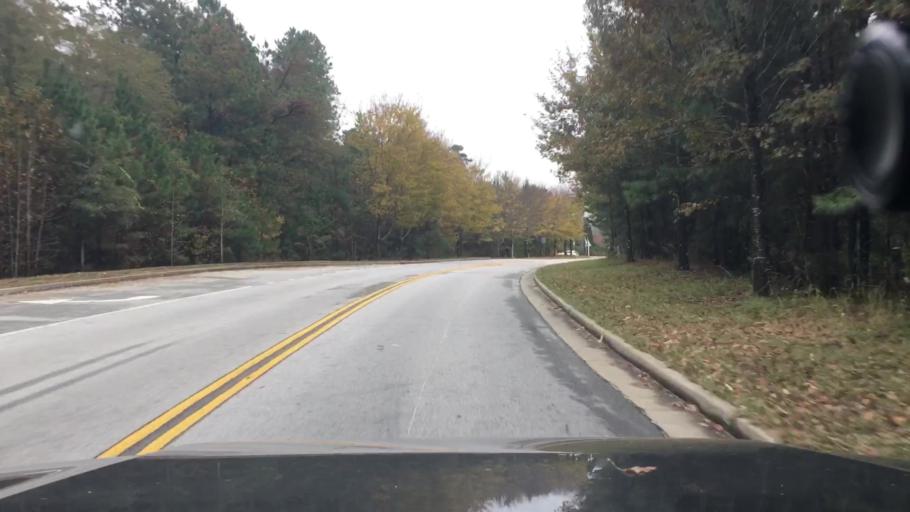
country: US
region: Georgia
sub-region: Coweta County
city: East Newnan
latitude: 33.3880
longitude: -84.7512
